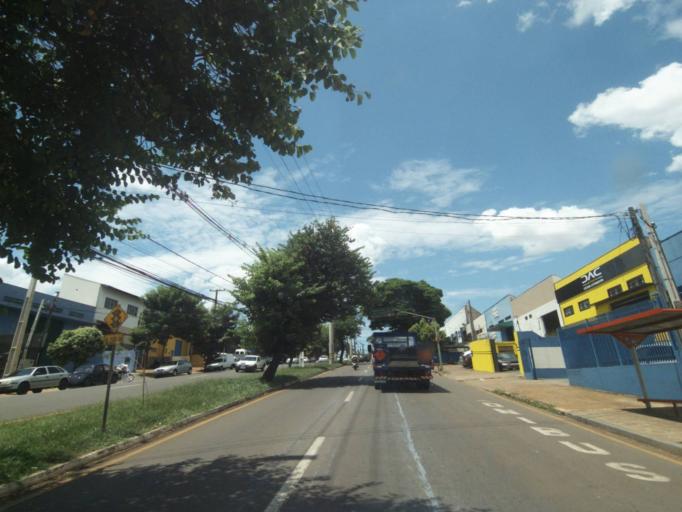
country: BR
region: Parana
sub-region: Londrina
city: Londrina
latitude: -23.3109
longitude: -51.2048
